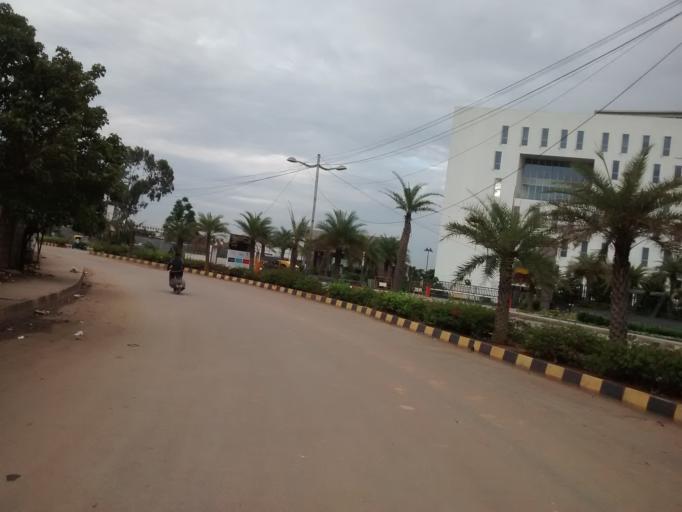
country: IN
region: Karnataka
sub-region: Bangalore Urban
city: Bangalore
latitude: 12.9491
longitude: 77.6888
